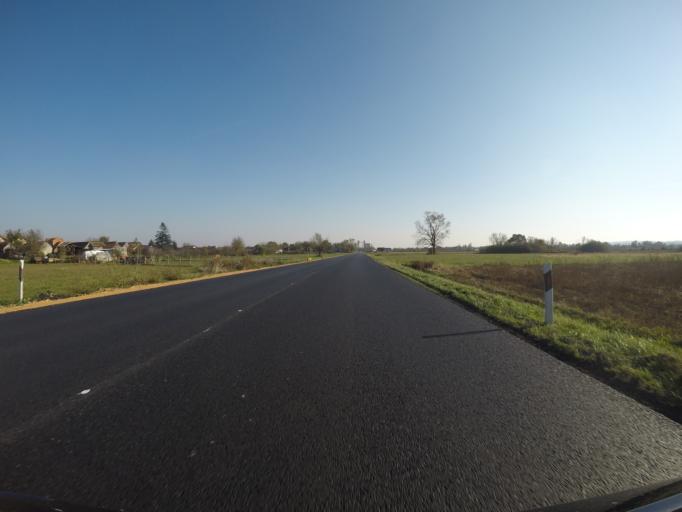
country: HR
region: Koprivnicko-Krizevacka
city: Kalinovac
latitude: 46.0383
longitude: 17.0561
